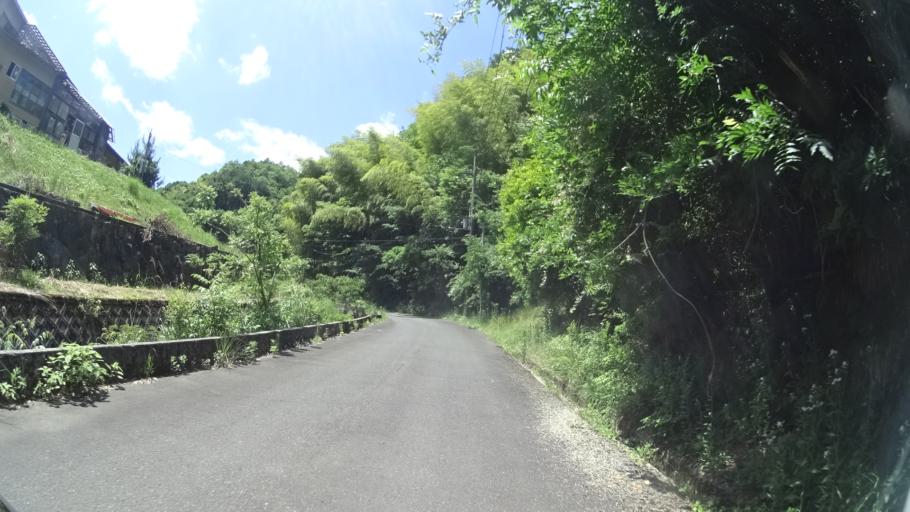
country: JP
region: Kyoto
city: Miyazu
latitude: 35.4416
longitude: 135.1794
